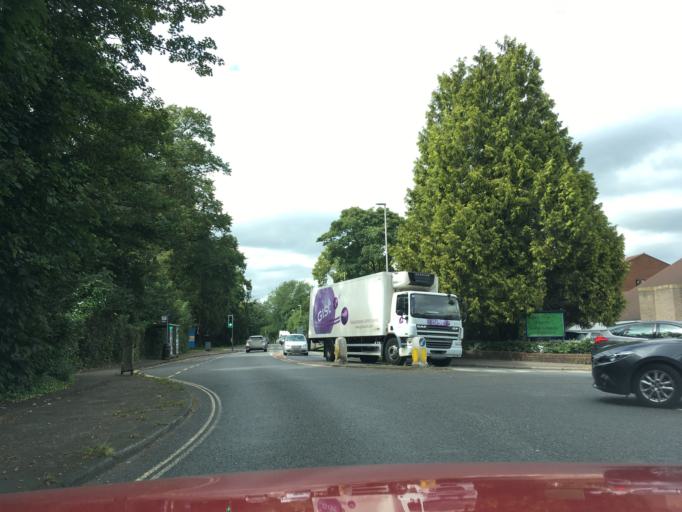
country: GB
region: England
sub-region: West Sussex
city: East Grinstead
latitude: 51.1308
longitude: -0.0186
